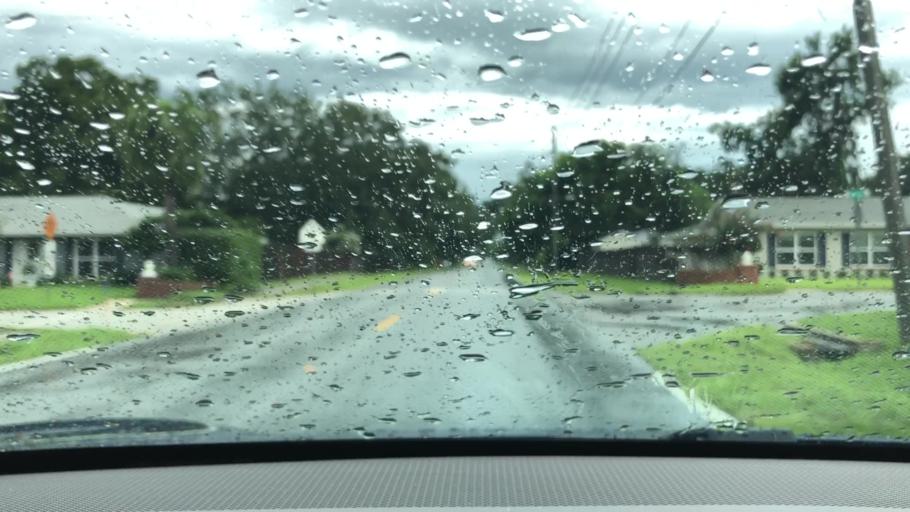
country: US
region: Florida
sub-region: Orange County
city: Conway
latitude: 28.5007
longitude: -81.3515
